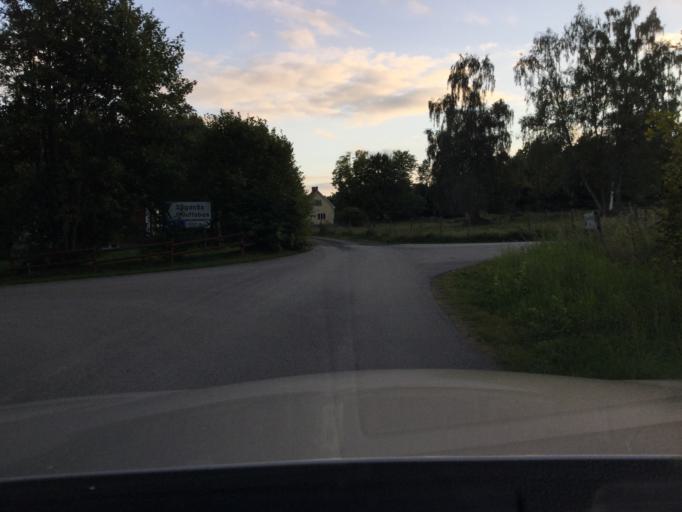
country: SE
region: Kronoberg
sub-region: Almhults Kommun
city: AElmhult
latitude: 56.6174
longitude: 14.2045
